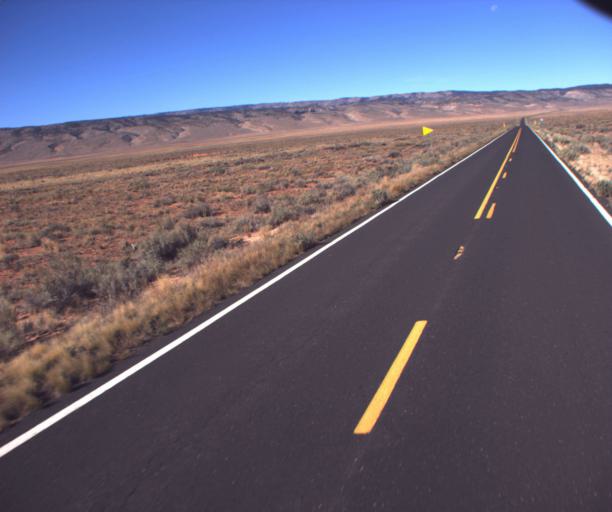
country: US
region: Arizona
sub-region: Coconino County
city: Page
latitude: 36.7132
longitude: -111.9824
